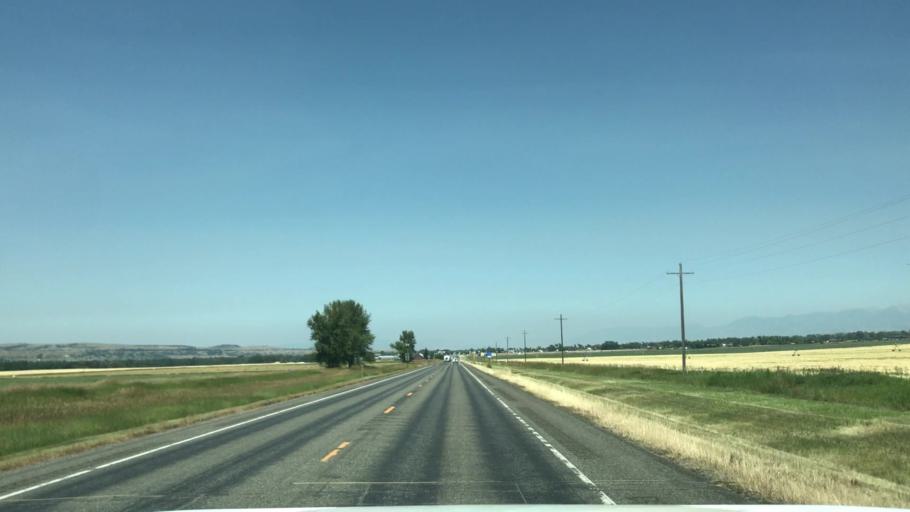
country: US
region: Montana
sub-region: Gallatin County
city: Four Corners
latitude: 45.5693
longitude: -111.1969
